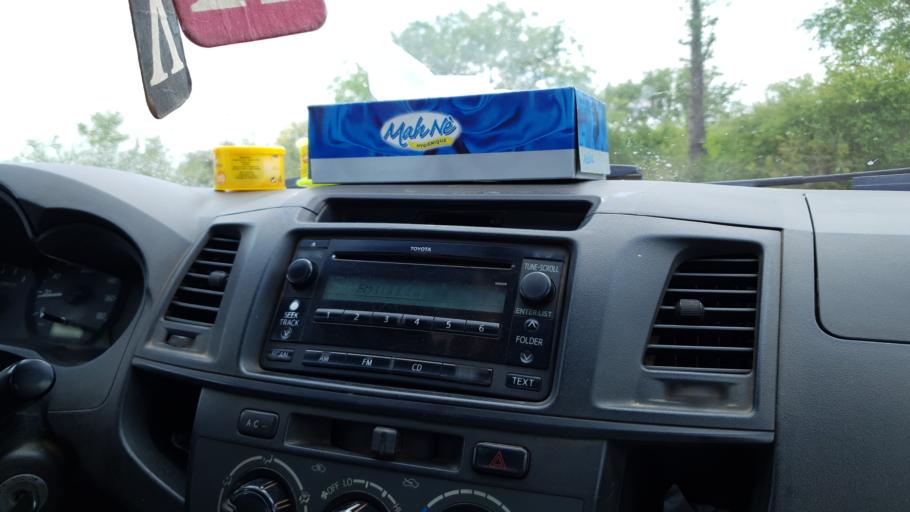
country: ML
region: Segou
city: Baroueli
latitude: 13.3480
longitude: -7.0944
